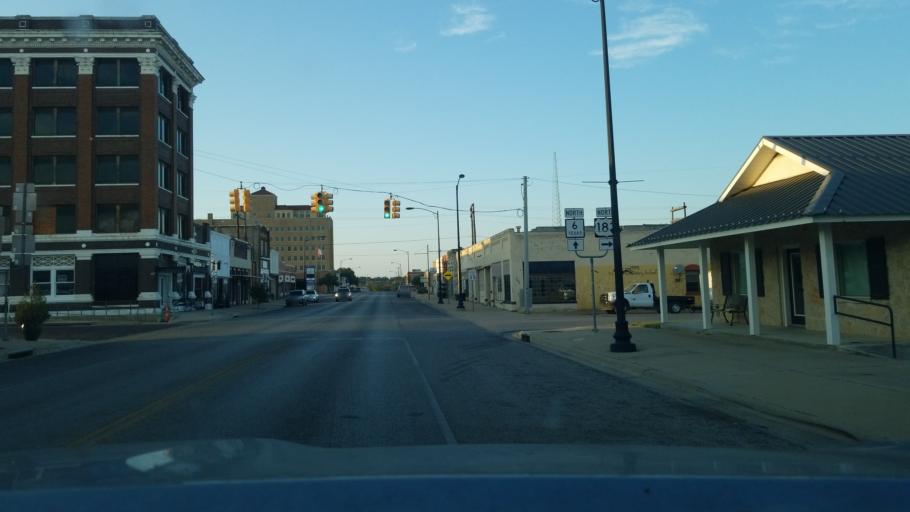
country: US
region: Texas
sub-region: Eastland County
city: Cisco
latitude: 32.3893
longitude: -98.9805
